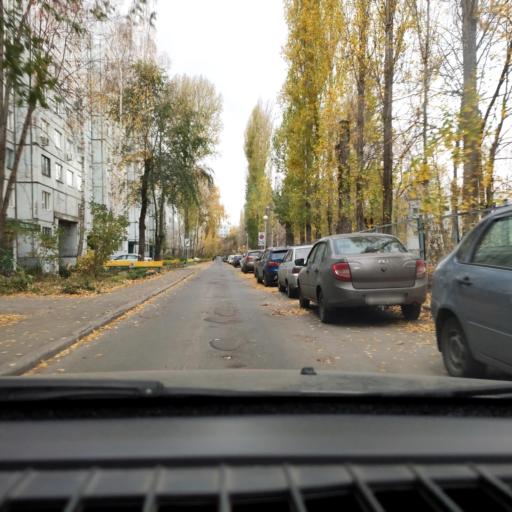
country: RU
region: Samara
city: Tol'yatti
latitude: 53.5256
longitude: 49.2891
